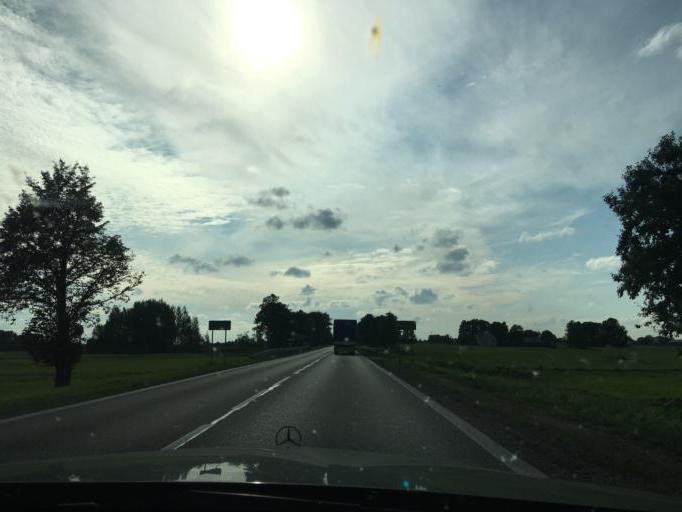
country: PL
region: Podlasie
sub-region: Powiat augustowski
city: Augustow
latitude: 53.8265
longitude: 22.9478
